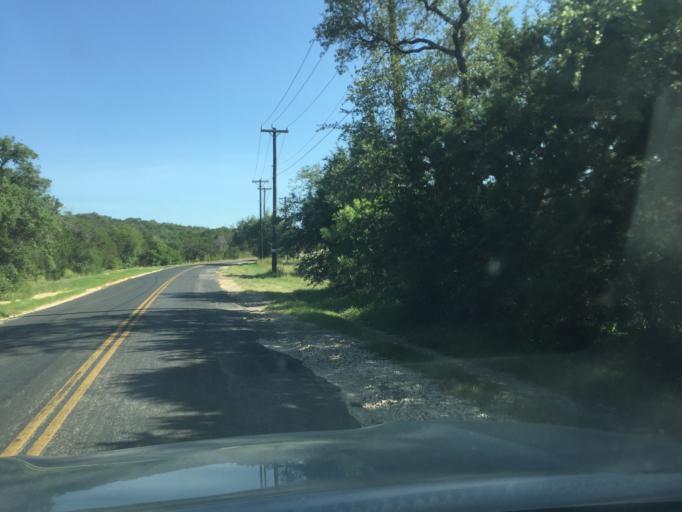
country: US
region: Texas
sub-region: Comal County
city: Bulverde
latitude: 29.7191
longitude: -98.4536
